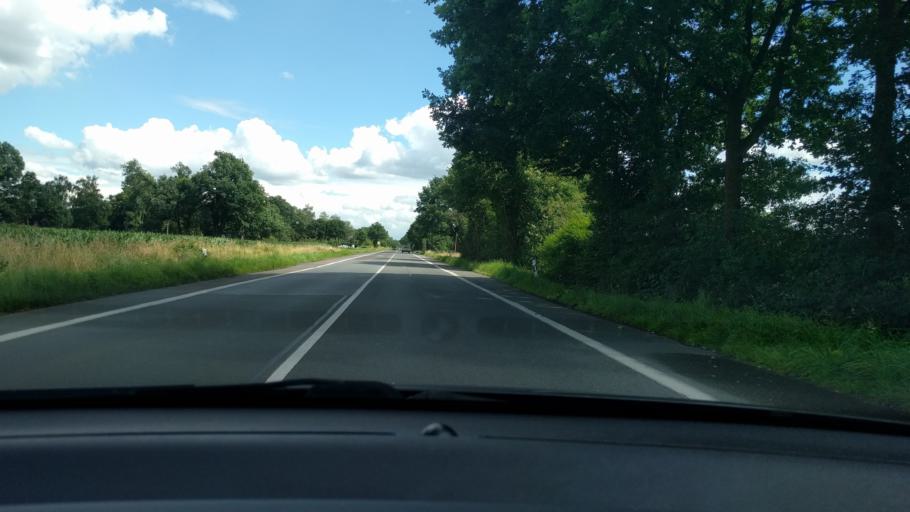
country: DE
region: North Rhine-Westphalia
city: Olfen
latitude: 51.6906
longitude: 7.3138
